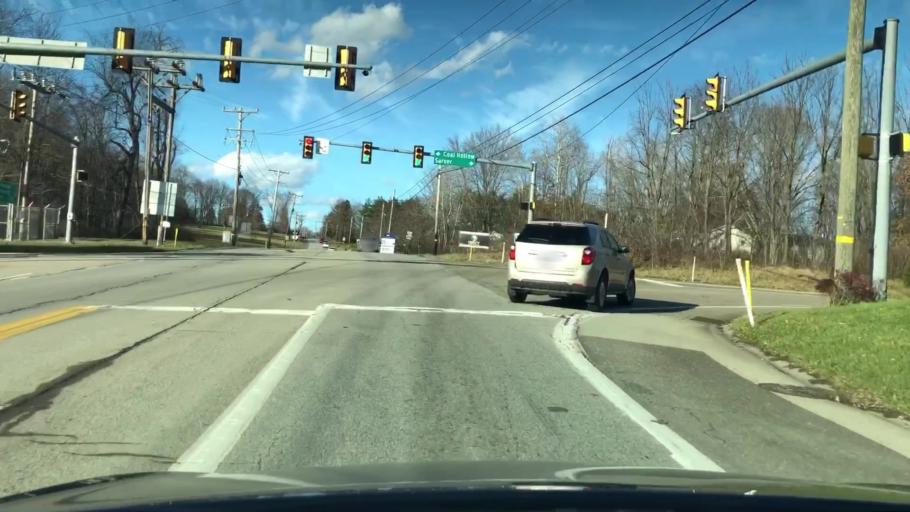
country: US
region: Pennsylvania
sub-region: Butler County
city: Saxonburg
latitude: 40.7239
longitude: -79.7565
